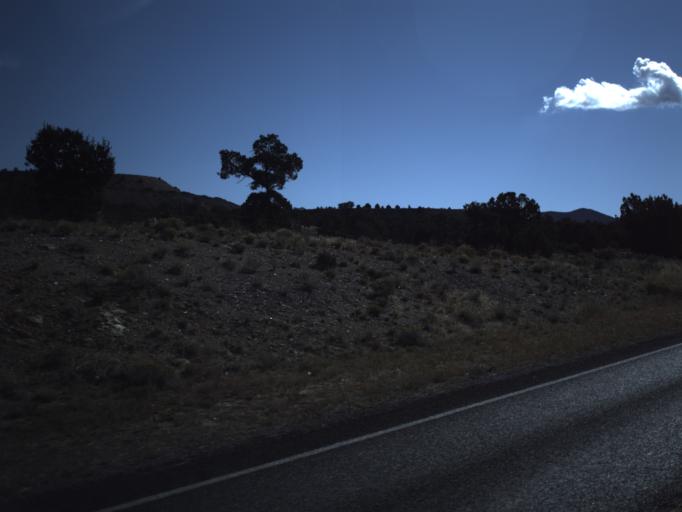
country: US
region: Utah
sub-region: Washington County
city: Enterprise
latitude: 37.6181
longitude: -113.4120
